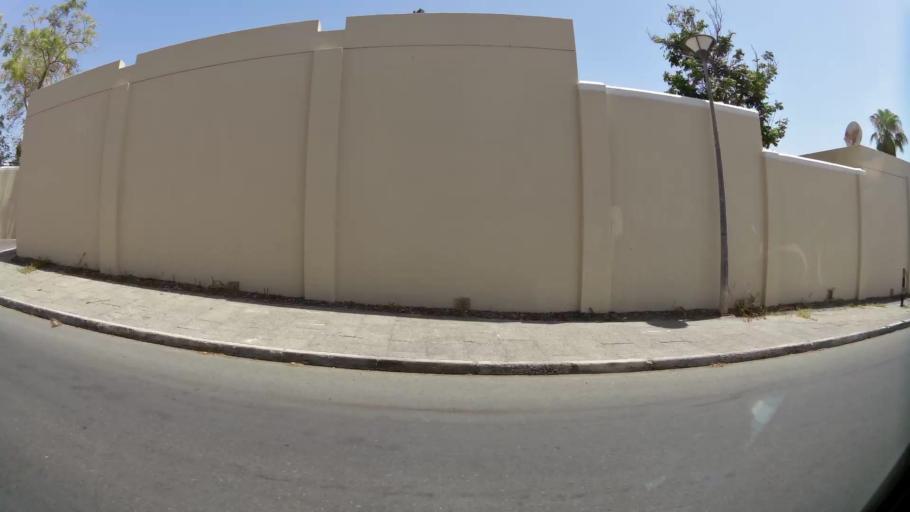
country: OM
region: Muhafazat Masqat
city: Muscat
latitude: 23.6319
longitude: 58.4836
